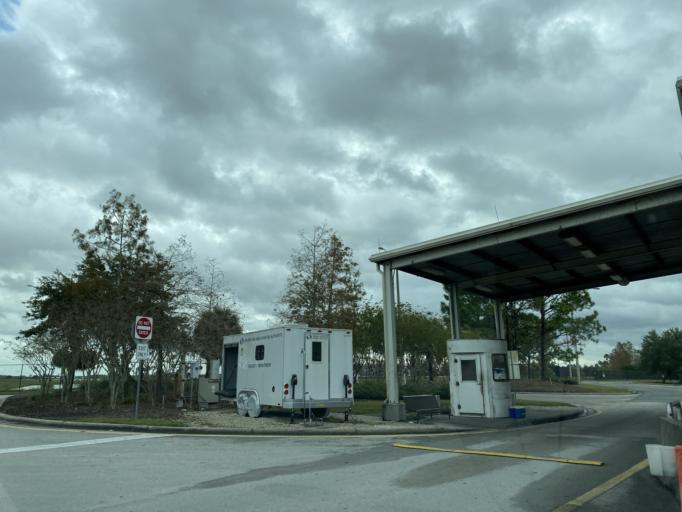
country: US
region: Florida
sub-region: Orange County
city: Belle Isle
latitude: 28.4383
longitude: -81.3071
